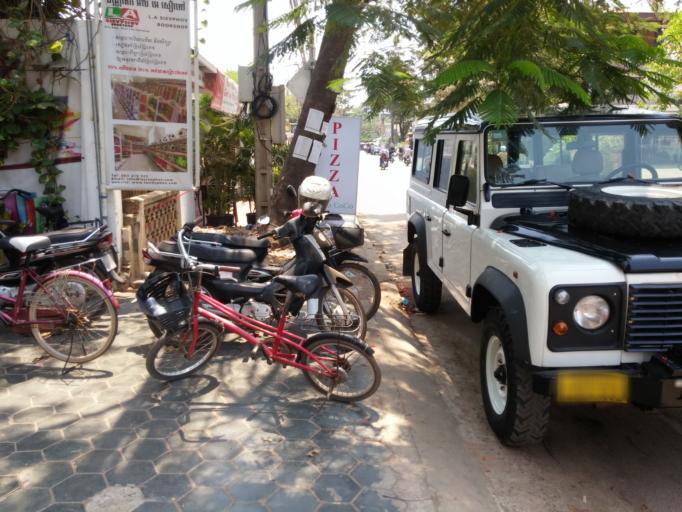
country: KH
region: Siem Reap
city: Siem Reap
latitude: 13.3552
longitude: 103.8595
